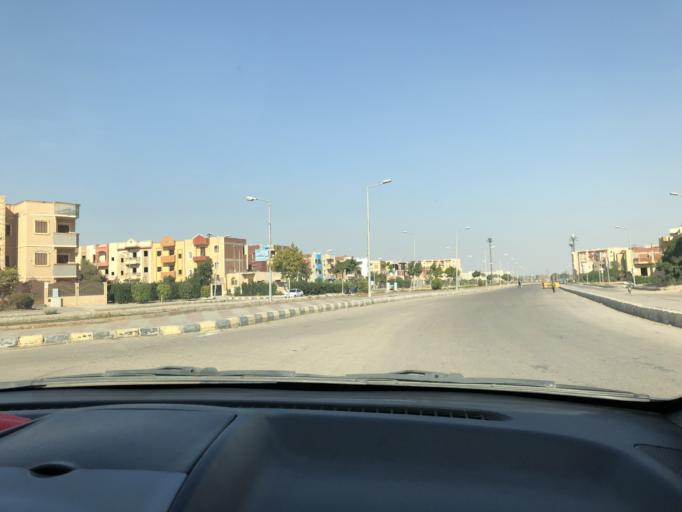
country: EG
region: Al Jizah
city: Madinat Sittah Uktubar
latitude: 29.9319
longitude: 31.0614
